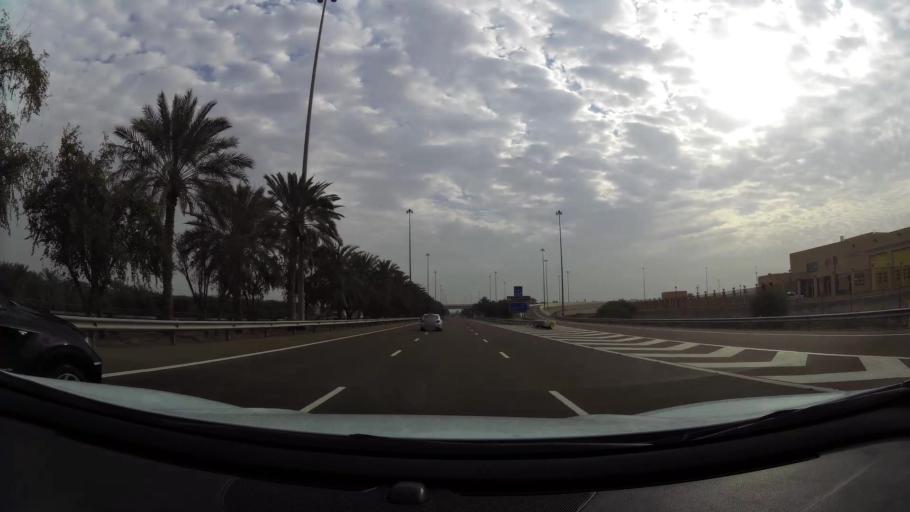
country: AE
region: Abu Dhabi
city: Al Ain
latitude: 24.1811
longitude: 55.3263
